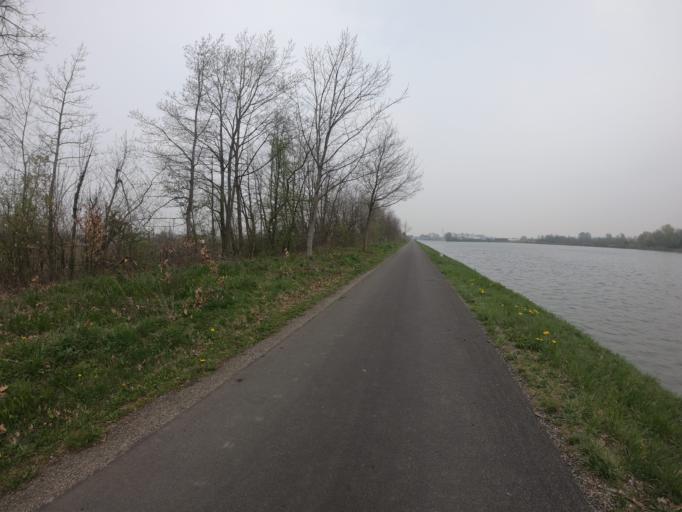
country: BE
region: Flanders
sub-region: Provincie Limburg
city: Maasmechelen
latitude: 50.9143
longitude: 5.6972
